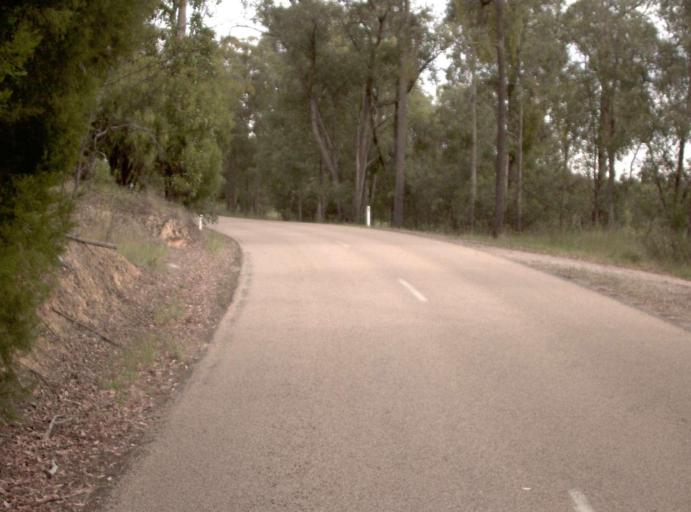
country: AU
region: Victoria
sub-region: East Gippsland
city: Bairnsdale
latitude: -37.7165
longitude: 147.5938
